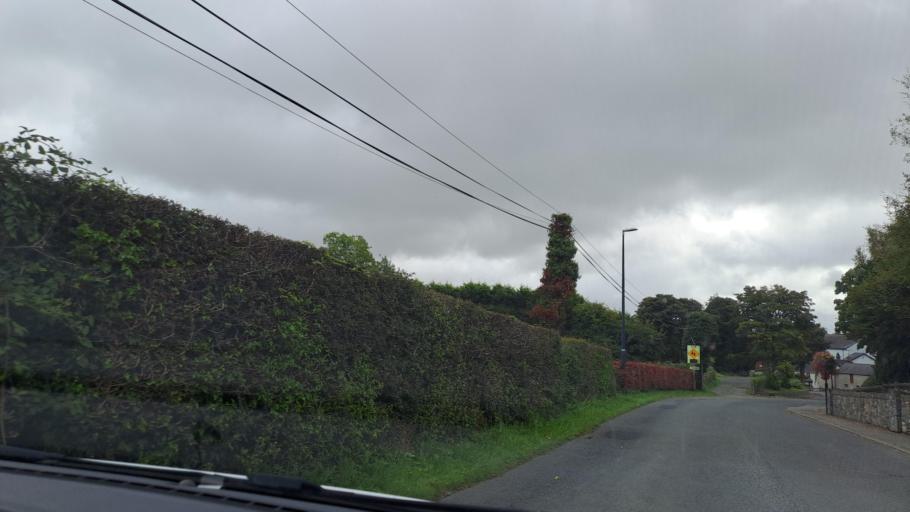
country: IE
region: Ulster
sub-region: County Monaghan
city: Carrickmacross
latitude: 54.0308
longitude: -6.7545
